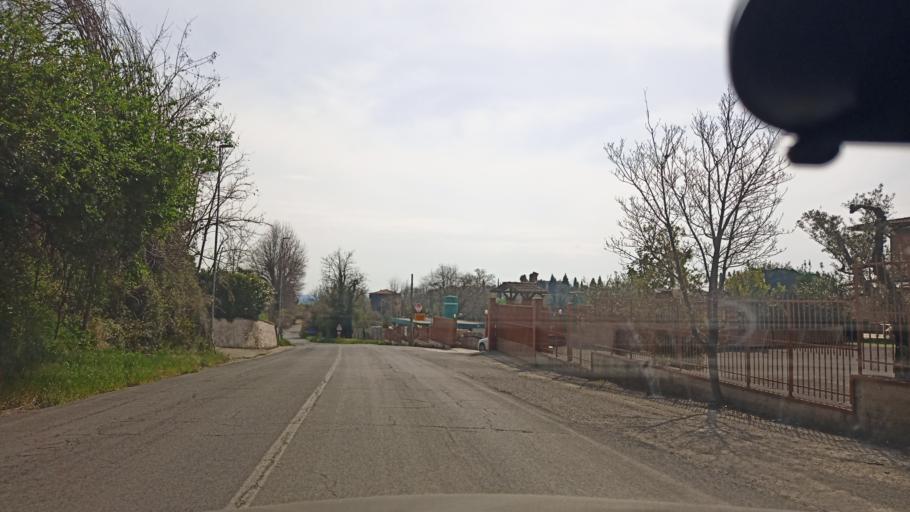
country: IT
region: Latium
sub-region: Provincia di Rieti
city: Cantalupo in Sabina
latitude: 42.3043
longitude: 12.6456
